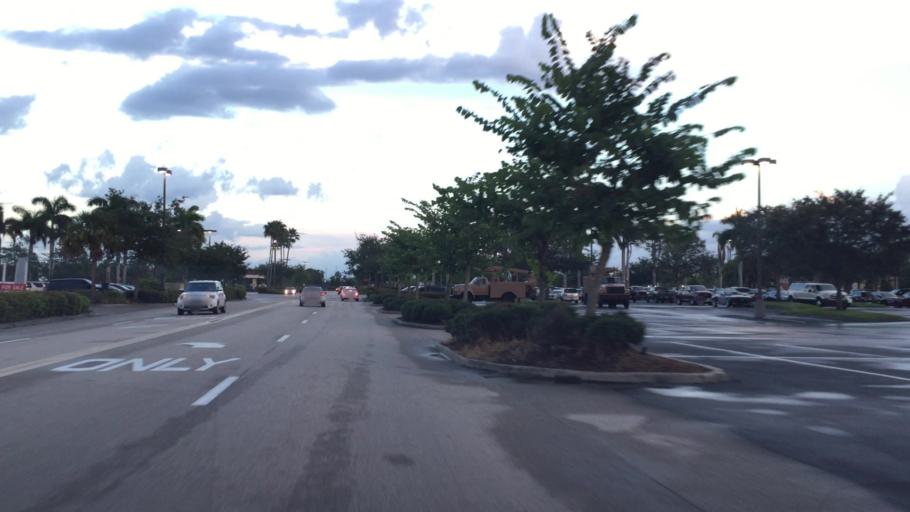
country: US
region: Florida
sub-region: Lee County
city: Three Oaks
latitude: 26.4891
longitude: -81.7887
